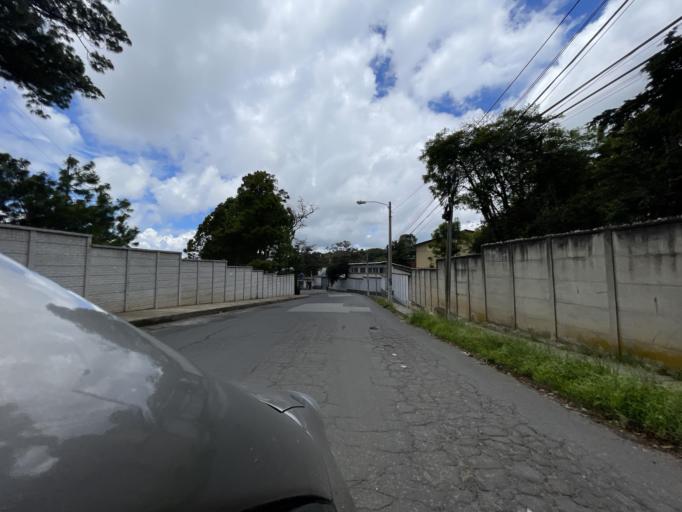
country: GT
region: Guatemala
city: Mixco
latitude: 14.6342
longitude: -90.6163
